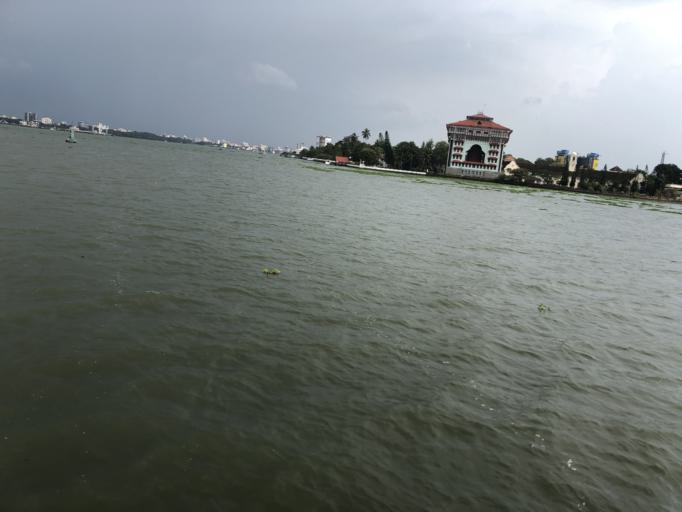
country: IN
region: Kerala
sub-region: Ernakulam
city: Cochin
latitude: 9.9720
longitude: 76.2564
